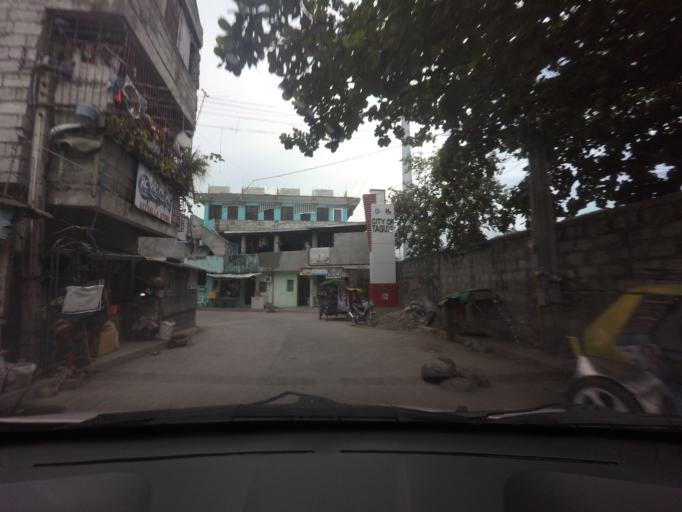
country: PH
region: Calabarzon
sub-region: Province of Rizal
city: Pateros
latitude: 14.5248
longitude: 121.0603
